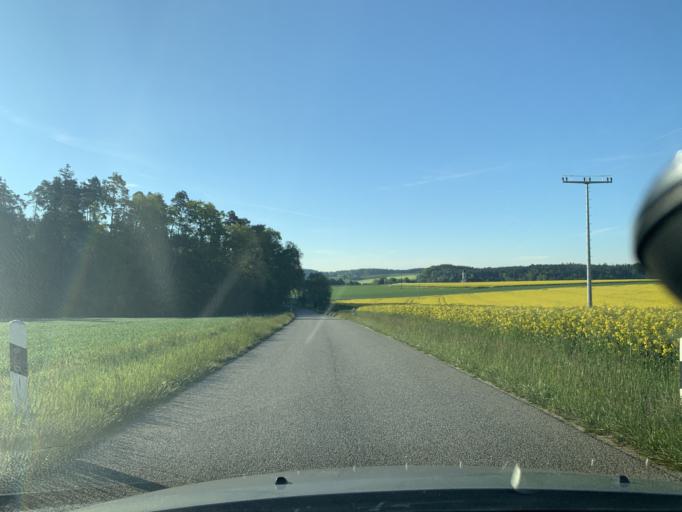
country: DE
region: Bavaria
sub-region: Lower Bavaria
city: Vilsbiburg
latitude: 48.5047
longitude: 12.3379
